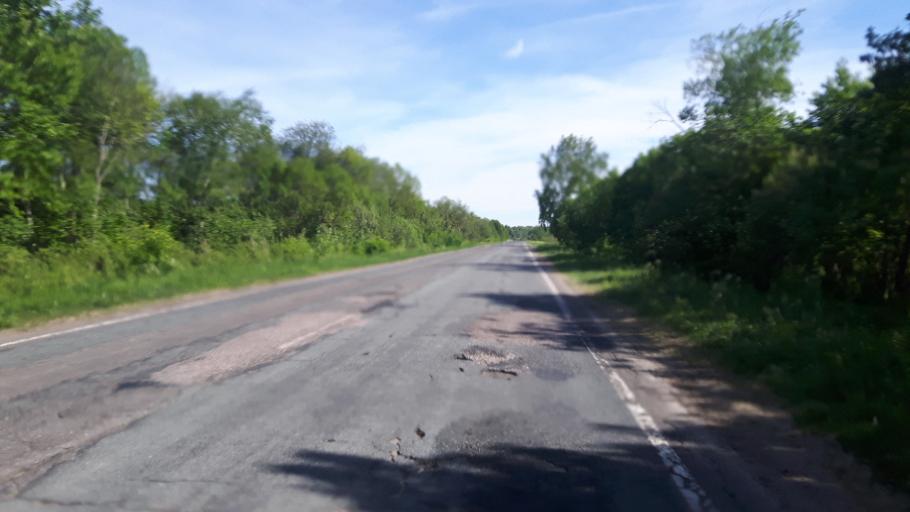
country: RU
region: Leningrad
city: Ivangorod
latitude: 59.4200
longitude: 28.3215
